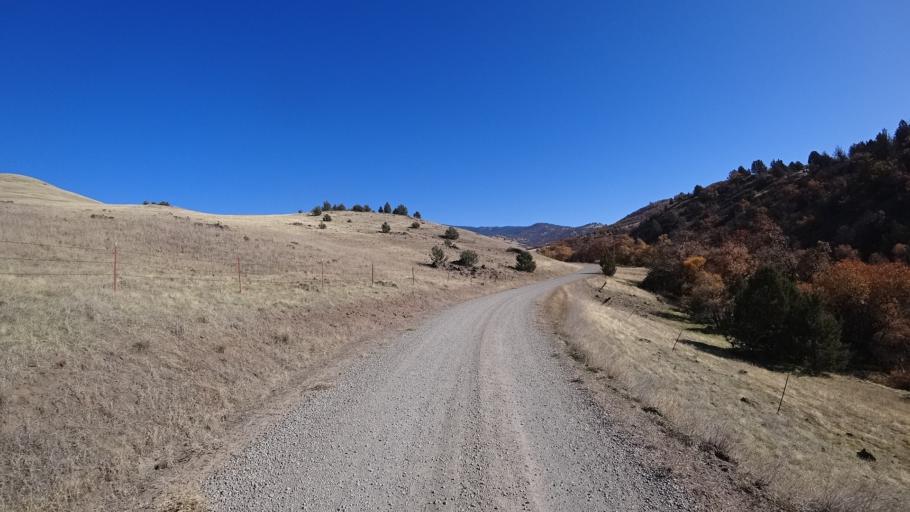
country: US
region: California
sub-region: Siskiyou County
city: Montague
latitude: 41.7936
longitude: -122.3453
